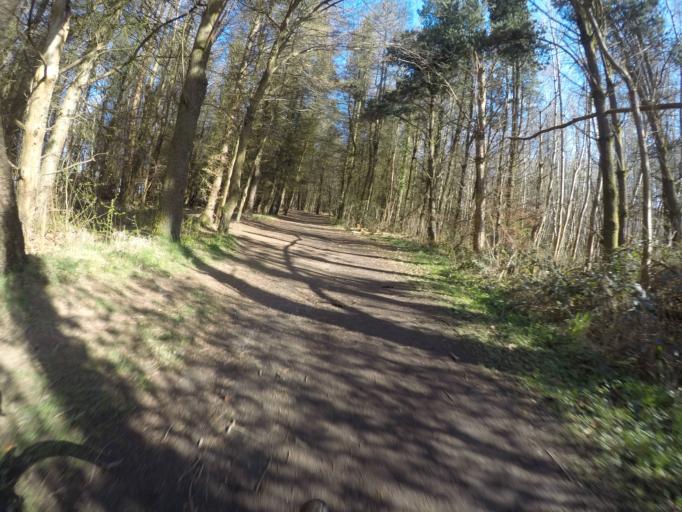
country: GB
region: Scotland
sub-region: North Ayrshire
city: Irvine
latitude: 55.6391
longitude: -4.6566
